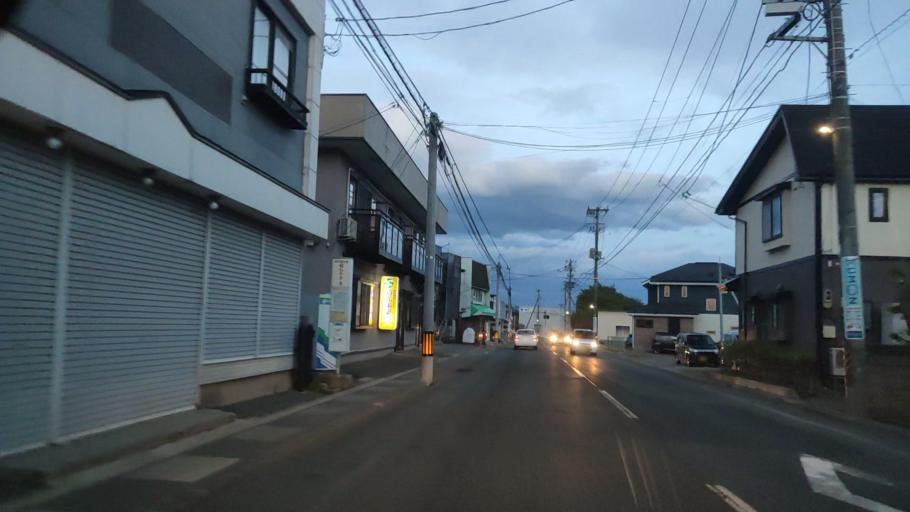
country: JP
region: Iwate
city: Morioka-shi
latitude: 39.7201
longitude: 141.1204
